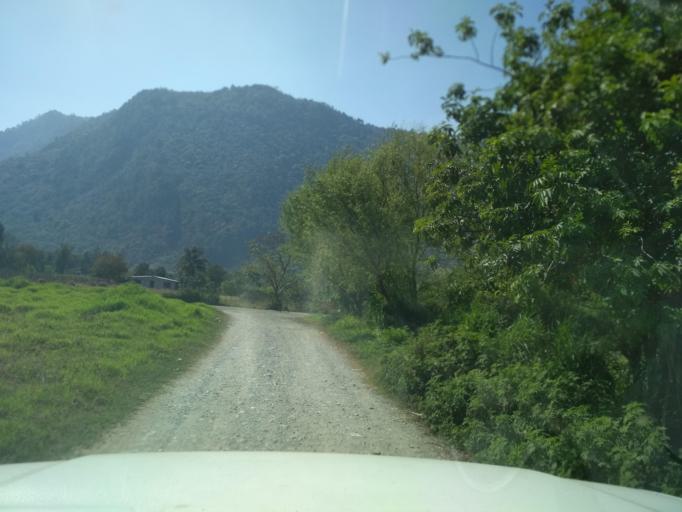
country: MX
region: Veracruz
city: Jalapilla
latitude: 18.8114
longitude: -97.0859
